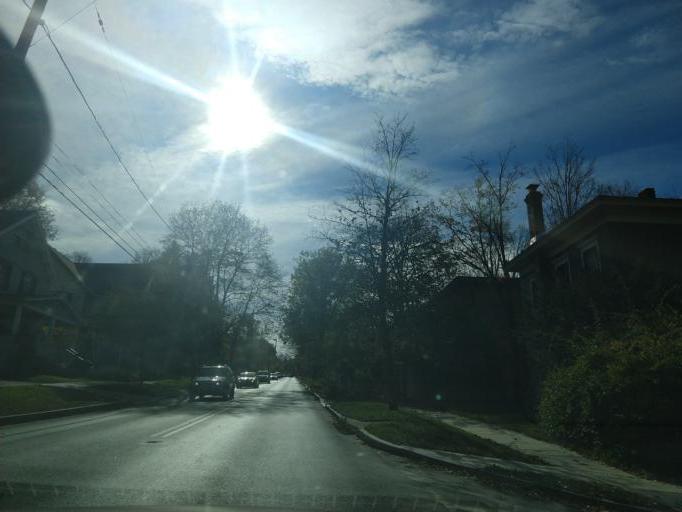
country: US
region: New York
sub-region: Tompkins County
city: Ithaca
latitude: 42.4367
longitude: -76.4948
